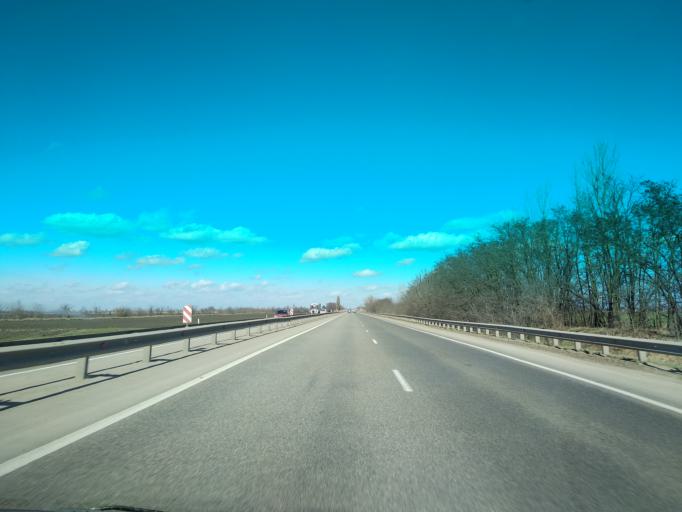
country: RU
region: Krasnodarskiy
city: Agronom
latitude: 45.1414
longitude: 39.1096
